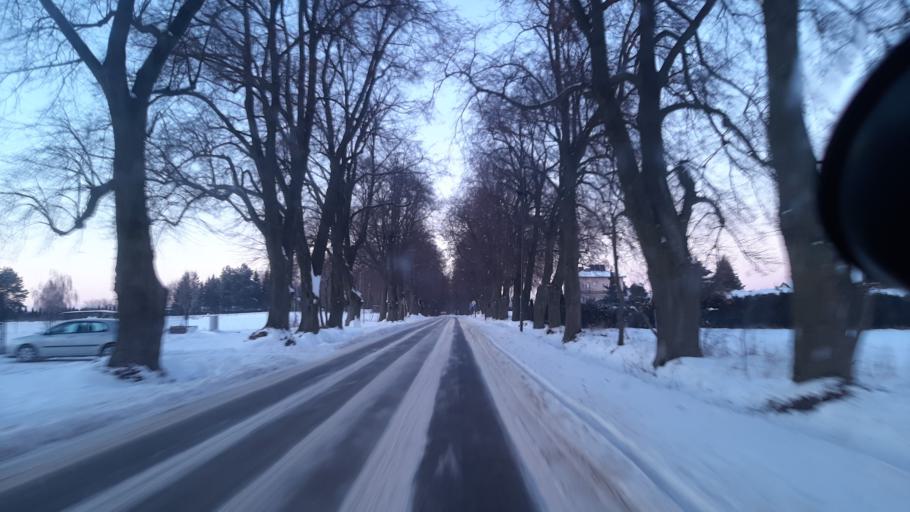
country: PL
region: Lublin Voivodeship
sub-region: Powiat lubelski
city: Lublin
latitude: 51.3230
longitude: 22.5609
